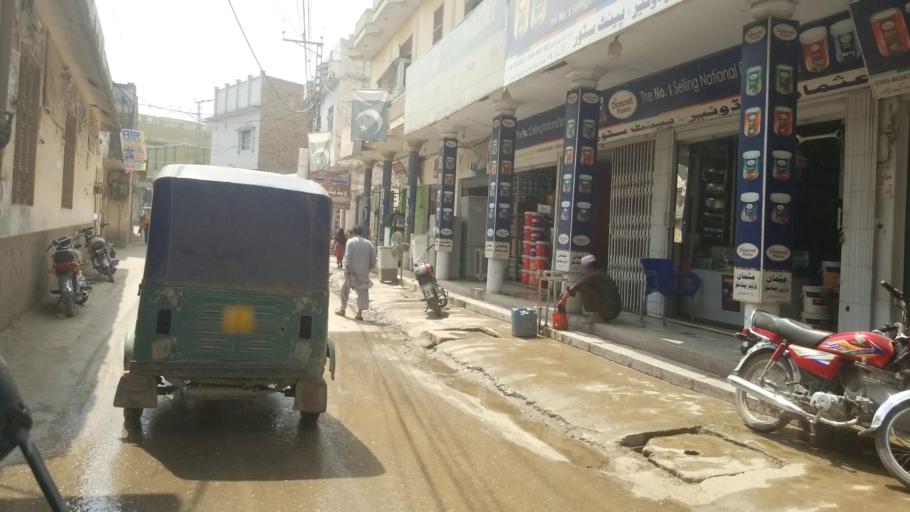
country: PK
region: Khyber Pakhtunkhwa
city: Peshawar
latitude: 33.9841
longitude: 71.5353
